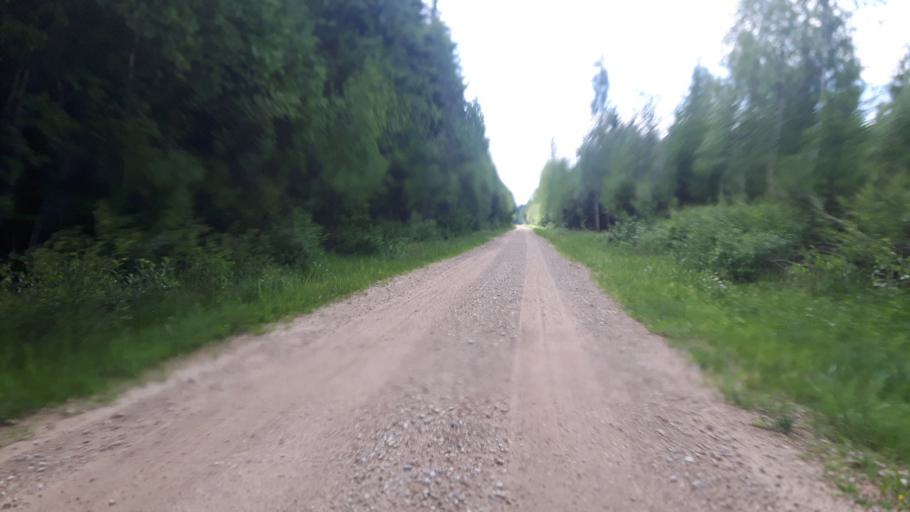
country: EE
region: Paernumaa
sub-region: Vaendra vald (alev)
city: Vandra
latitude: 58.7341
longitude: 25.0020
